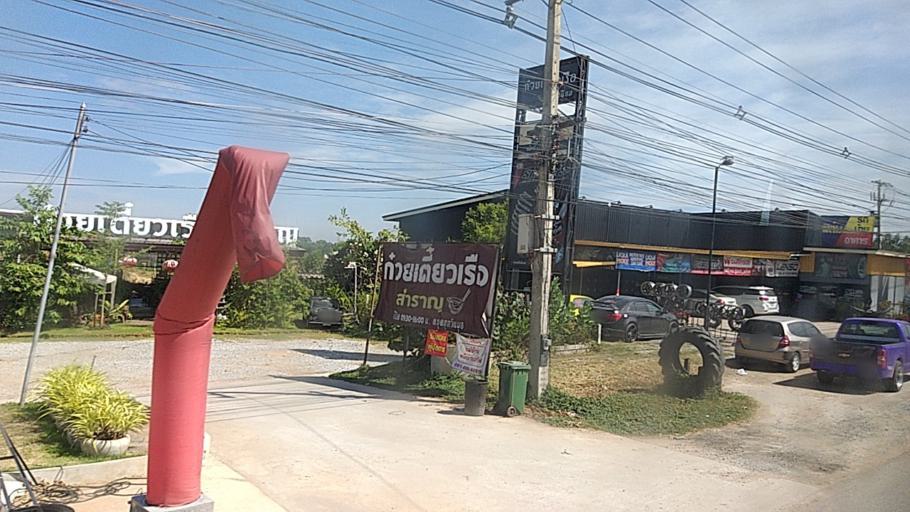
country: TH
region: Khon Kaen
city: Khon Kaen
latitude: 16.4378
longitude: 102.9309
